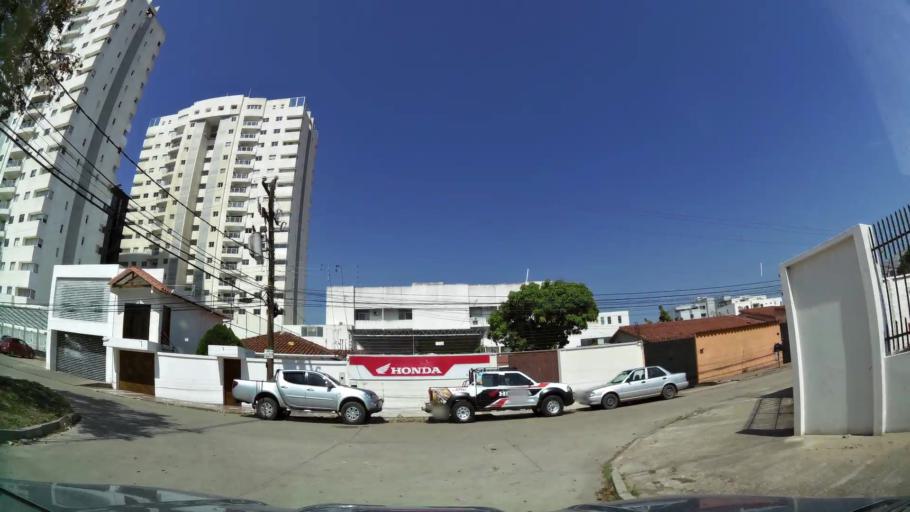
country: BO
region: Santa Cruz
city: Santa Cruz de la Sierra
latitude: -17.7478
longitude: -63.1692
